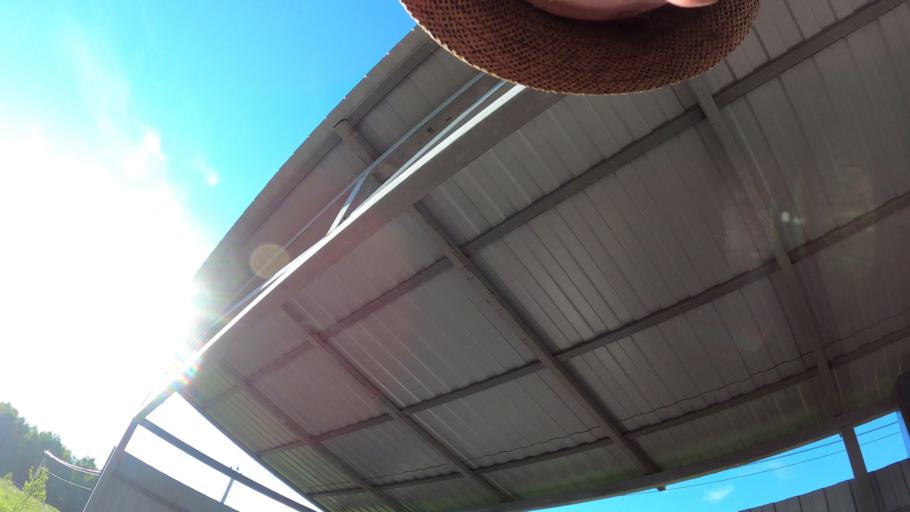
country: RU
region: Moskovskaya
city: Ashitkovo
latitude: 55.4427
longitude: 38.6055
